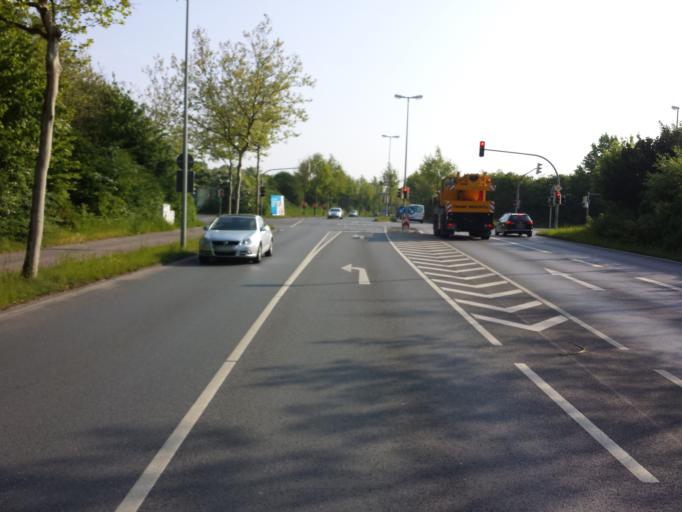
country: DE
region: North Rhine-Westphalia
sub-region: Regierungsbezirk Detmold
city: Guetersloh
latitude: 51.8862
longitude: 8.3886
